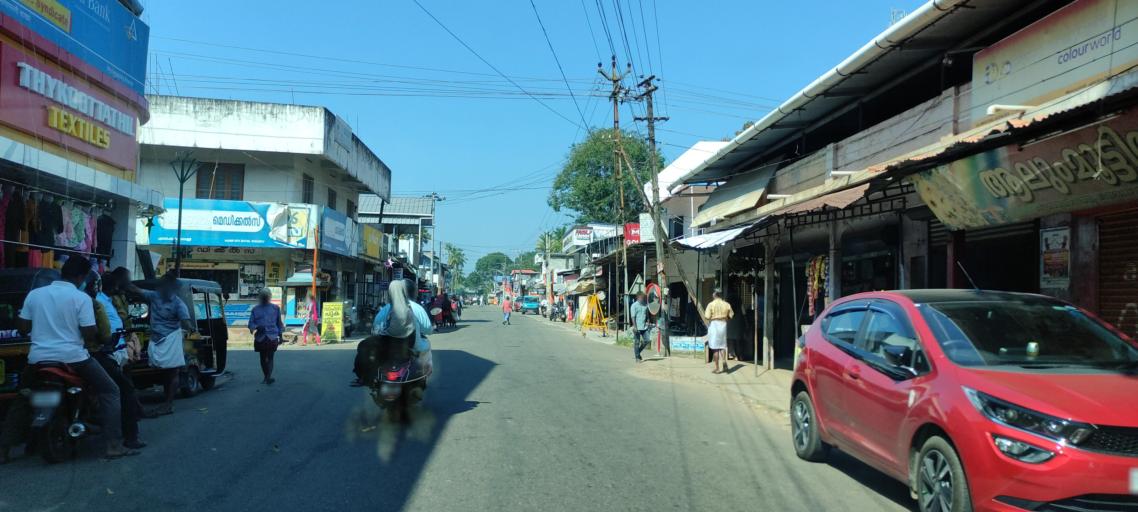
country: IN
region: Kerala
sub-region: Kollam
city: Panmana
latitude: 9.0425
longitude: 76.5835
